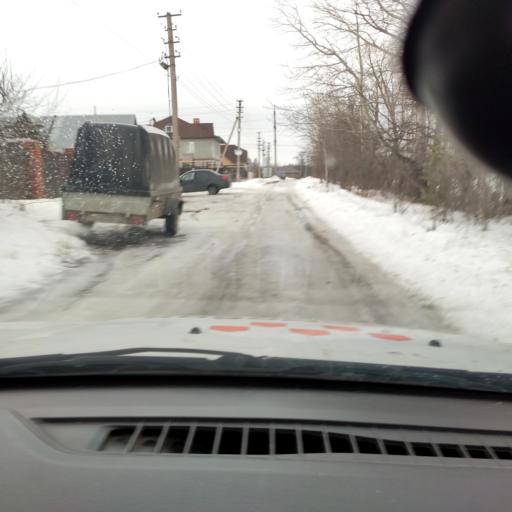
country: RU
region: Bashkortostan
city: Ufa
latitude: 54.5266
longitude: 55.9185
